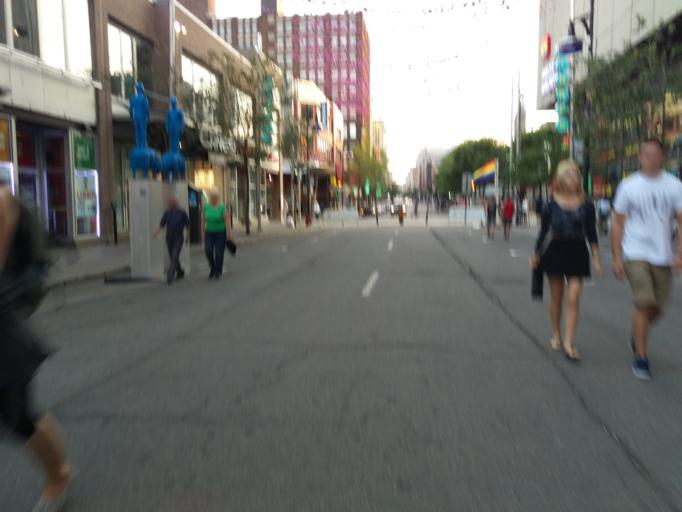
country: CA
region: Quebec
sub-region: Montreal
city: Montreal
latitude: 45.5158
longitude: -73.5587
